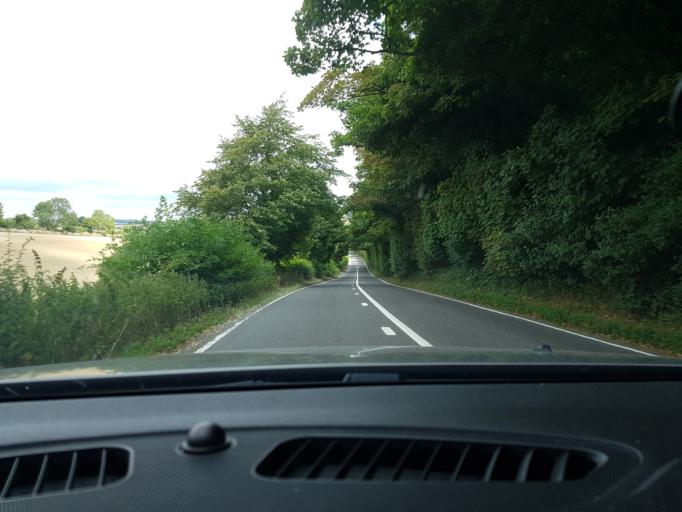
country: GB
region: England
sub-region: West Berkshire
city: Wickham
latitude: 51.4676
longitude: -1.4581
